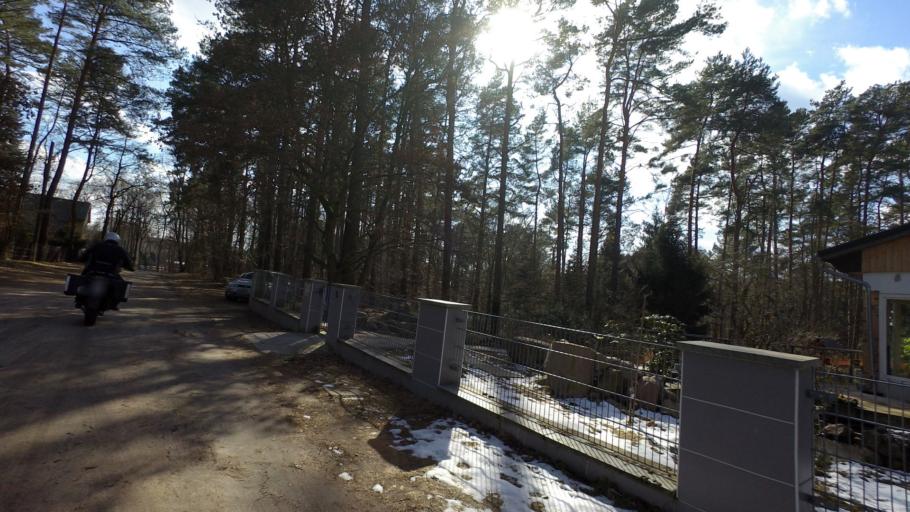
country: DE
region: Brandenburg
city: Biesenthal
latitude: 52.7695
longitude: 13.6135
